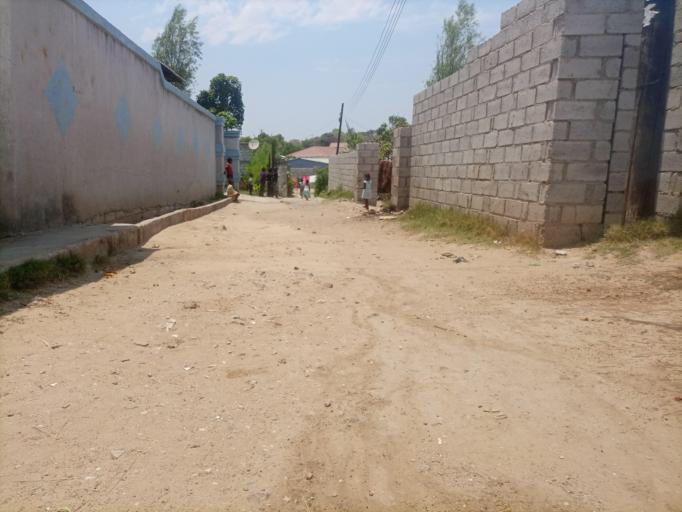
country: ZM
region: Lusaka
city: Lusaka
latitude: -15.4093
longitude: 28.3761
